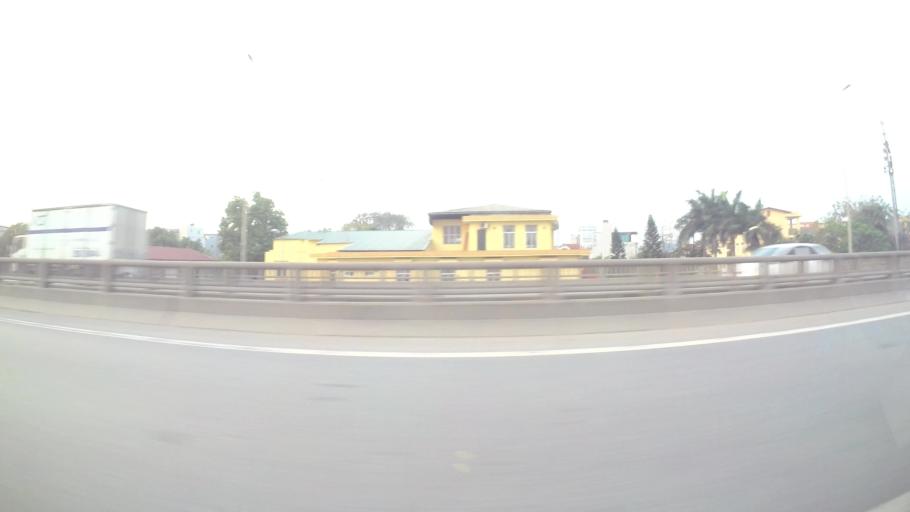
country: VN
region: Ha Noi
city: Van Dien
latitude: 20.9659
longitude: 105.8379
